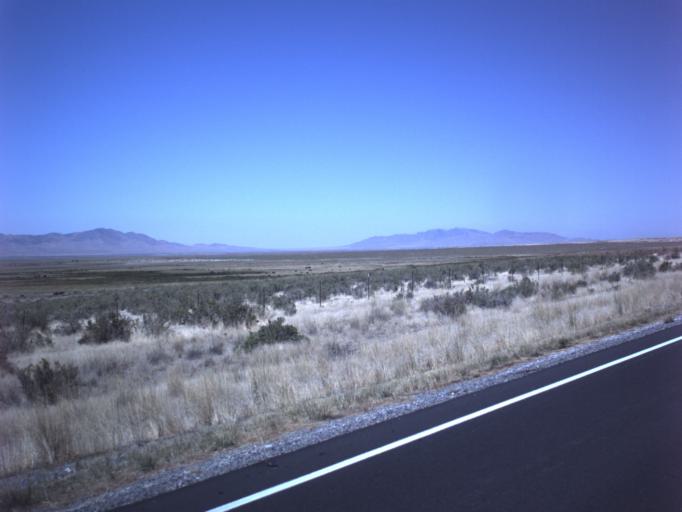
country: US
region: Utah
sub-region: Tooele County
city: Grantsville
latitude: 40.5563
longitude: -112.7376
